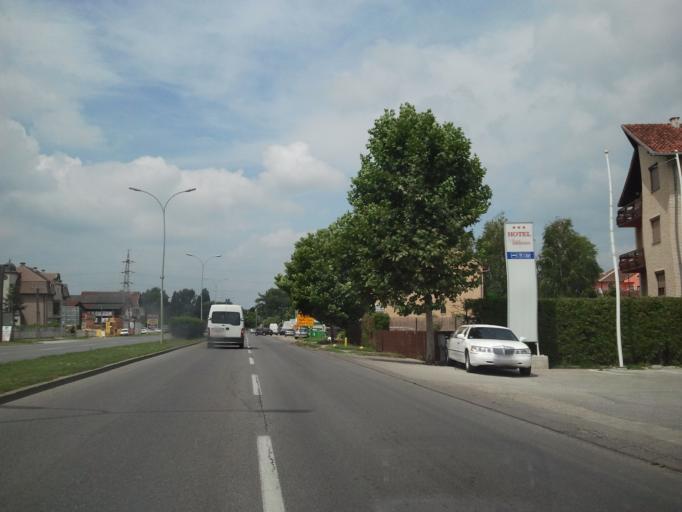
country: RS
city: Veternik
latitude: 45.2438
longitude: 19.7814
